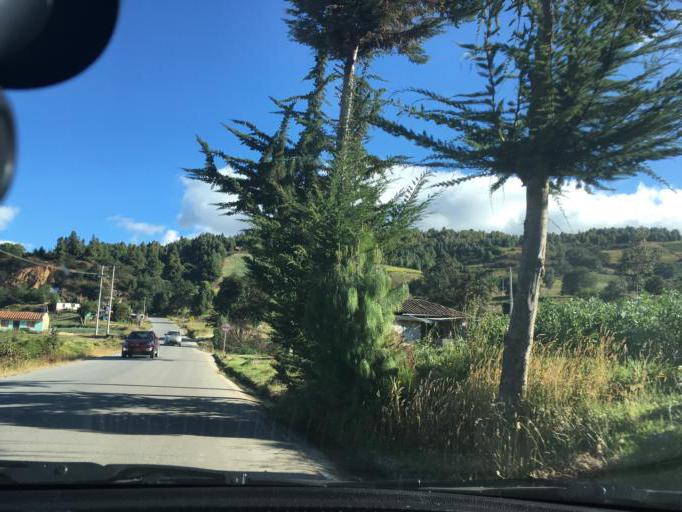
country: CO
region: Boyaca
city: Pesca
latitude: 5.5117
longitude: -72.9742
